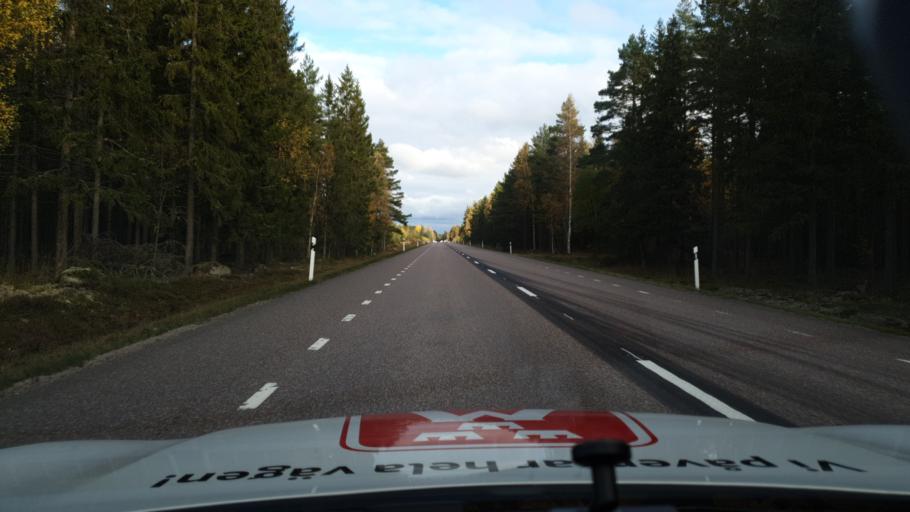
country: SE
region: Gaevleborg
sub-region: Gavle Kommun
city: Hedesunda
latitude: 60.3080
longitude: 16.9151
